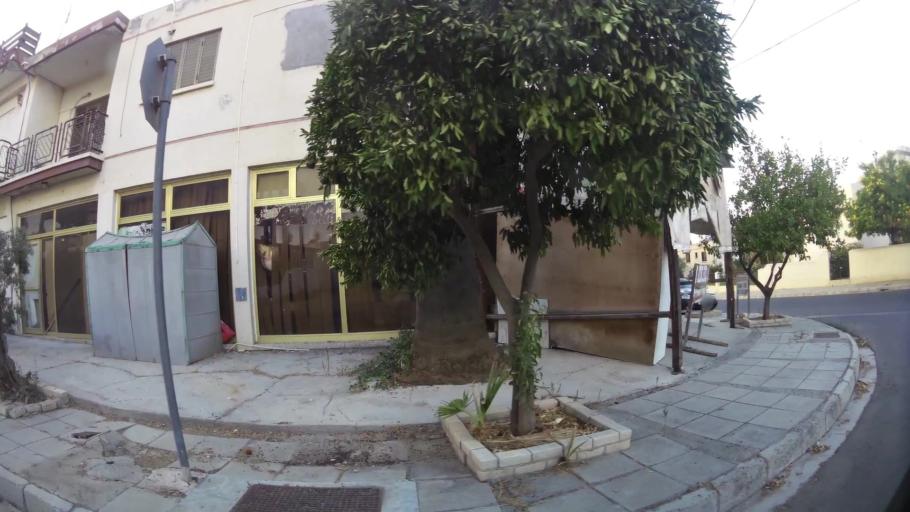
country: CY
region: Lefkosia
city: Tseri
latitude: 35.1154
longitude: 33.3185
